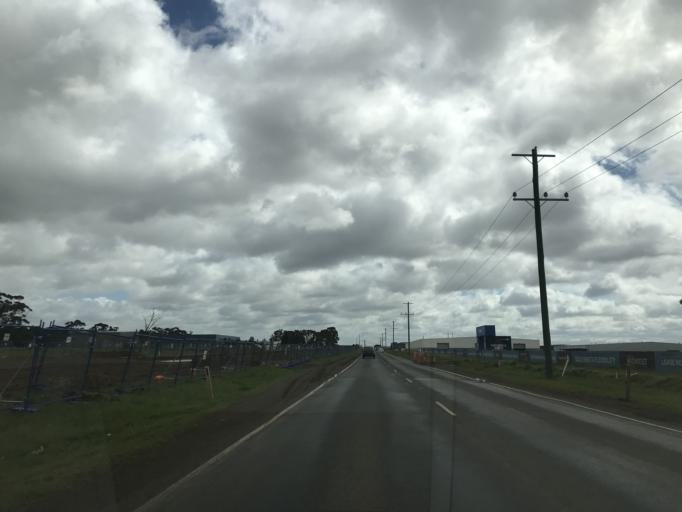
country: AU
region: Victoria
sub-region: Wyndham
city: Truganina
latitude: -37.8228
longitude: 144.7492
